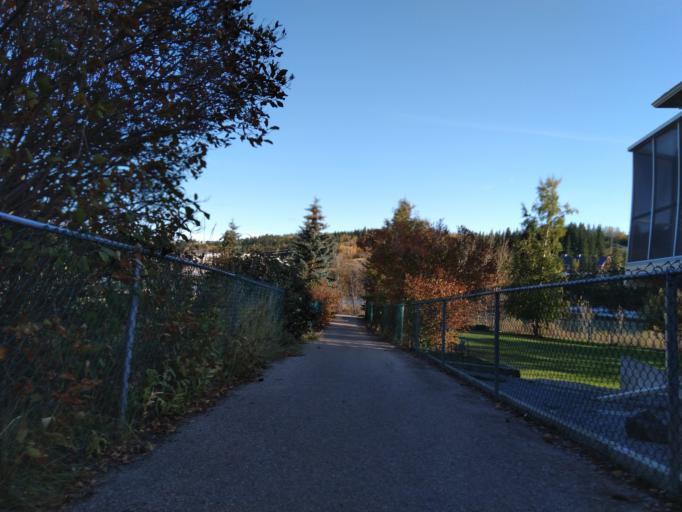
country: CA
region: Alberta
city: Cochrane
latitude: 51.1737
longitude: -114.4699
